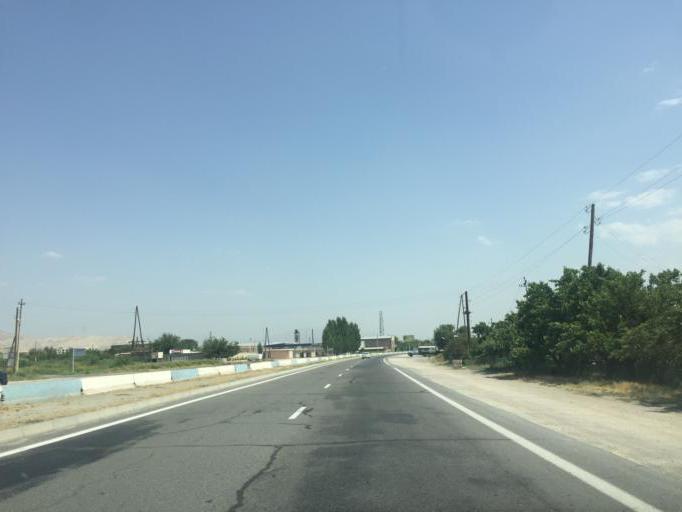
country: AM
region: Ararat
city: Artashat
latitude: 39.9558
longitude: 44.5343
